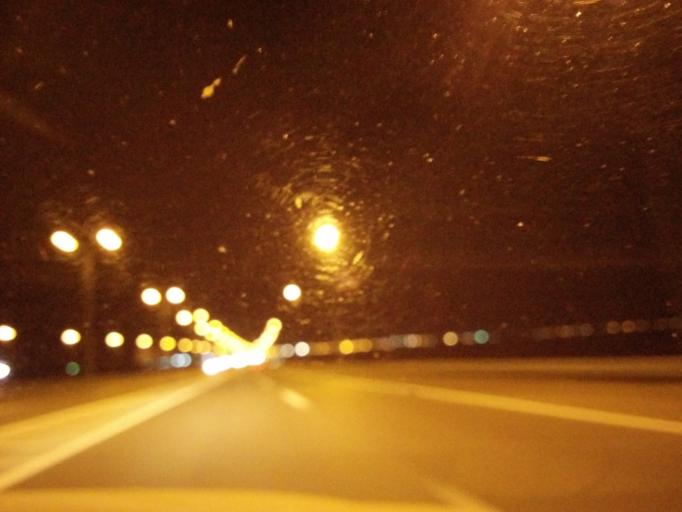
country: RS
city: Dobanovci
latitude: 44.8383
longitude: 20.2369
